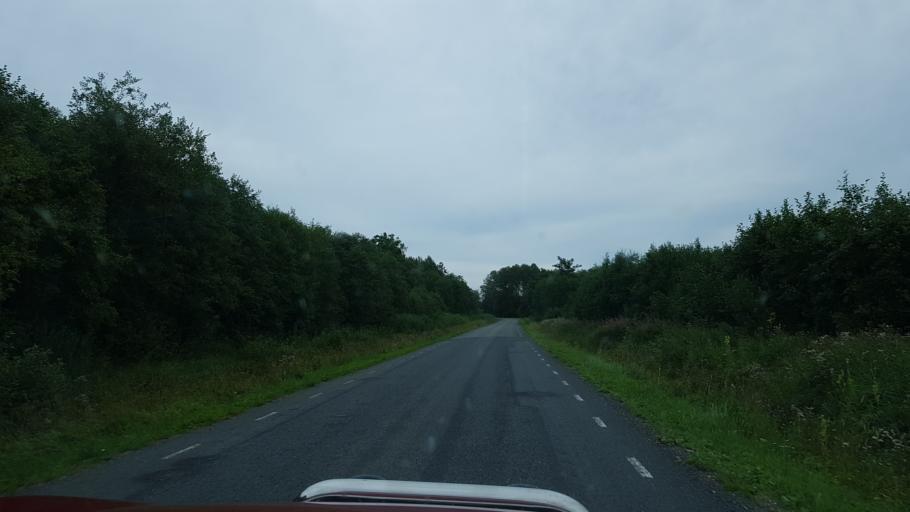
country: EE
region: Laeaene
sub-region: Lihula vald
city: Lihula
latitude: 58.8736
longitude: 23.8896
